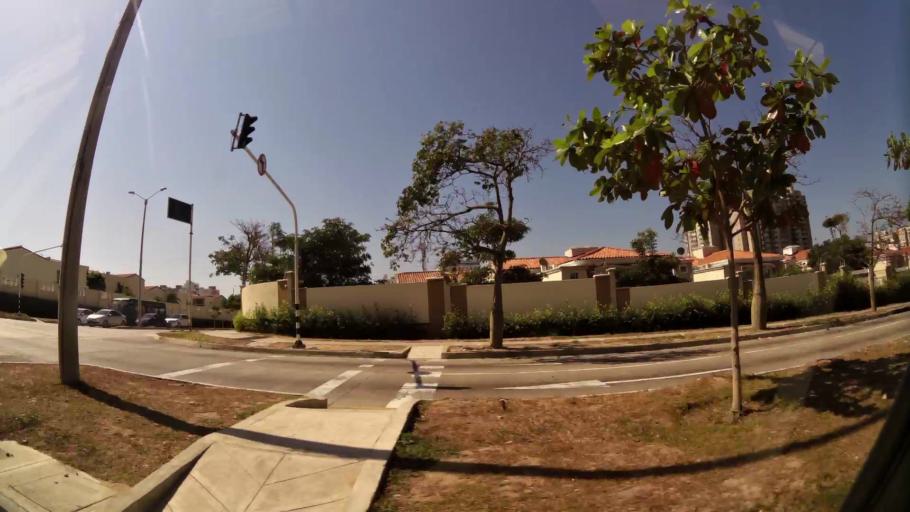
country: CO
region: Atlantico
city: Barranquilla
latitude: 11.0178
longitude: -74.8350
